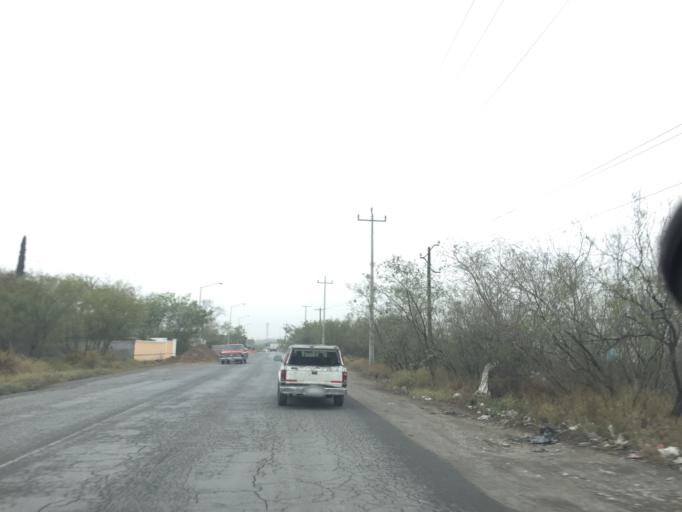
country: MX
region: Nuevo Leon
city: Mina
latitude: 25.9752
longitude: -100.4427
